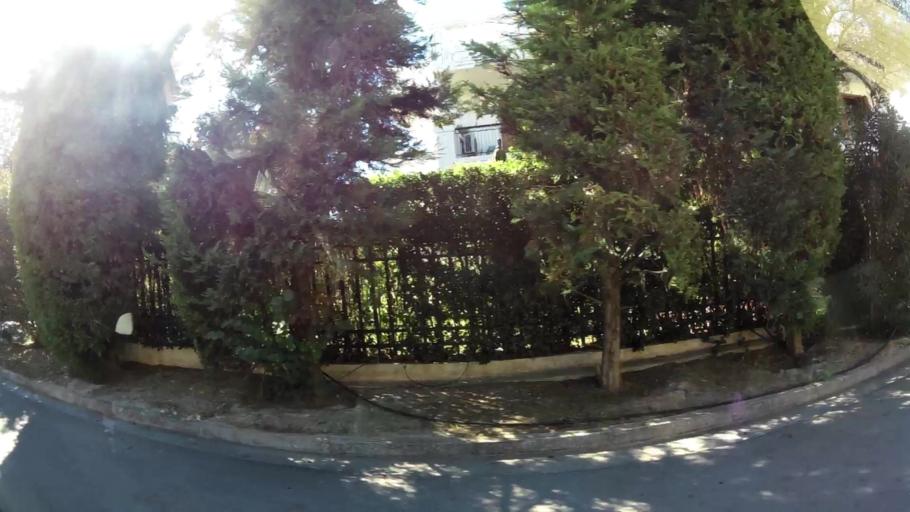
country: GR
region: Attica
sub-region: Nomarchia Athinas
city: Kifisia
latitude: 38.0846
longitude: 23.8013
